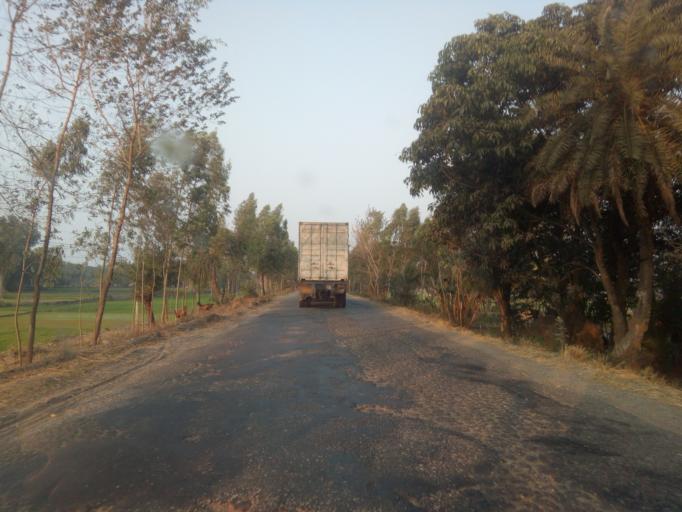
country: BD
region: Rajshahi
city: Par Naogaon
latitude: 24.5488
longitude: 89.1903
